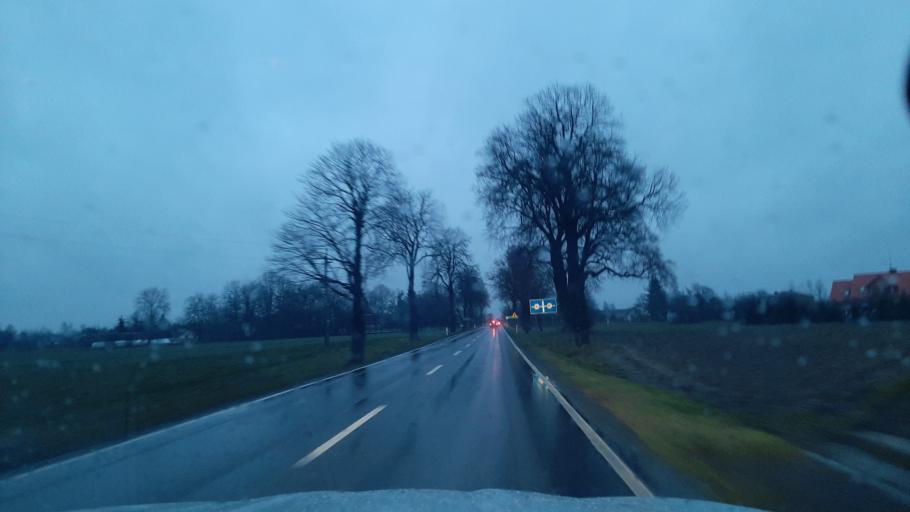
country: PL
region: Lublin Voivodeship
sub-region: Powiat lubelski
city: Jastkow
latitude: 51.3450
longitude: 22.4856
